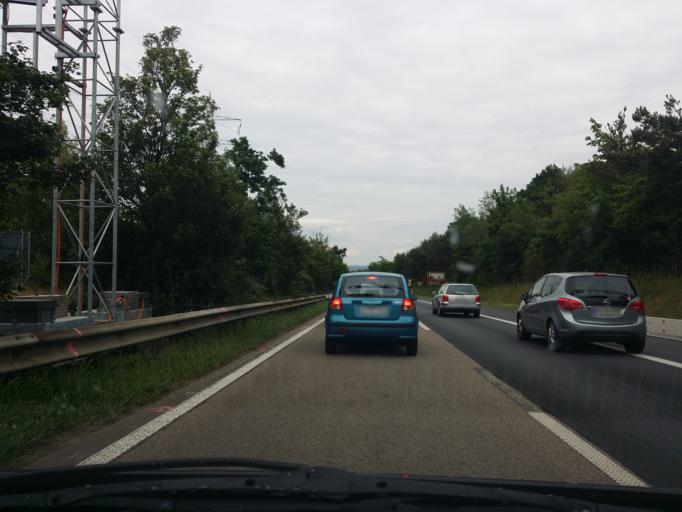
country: DE
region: Rheinland-Pfalz
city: Budenheim
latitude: 50.0147
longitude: 8.2047
